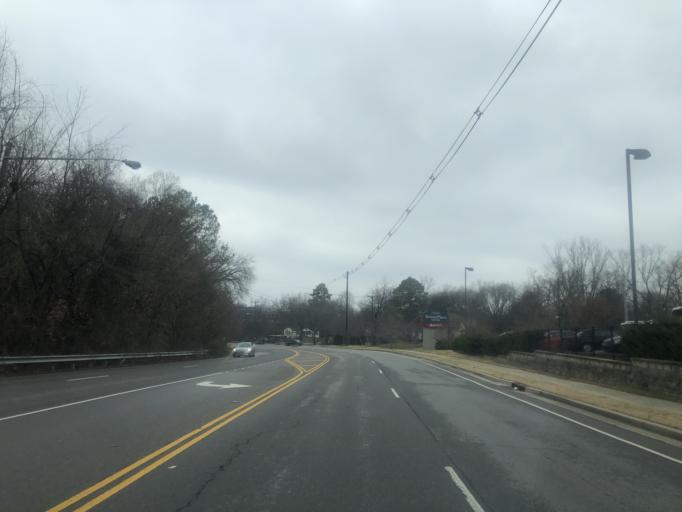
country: US
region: Tennessee
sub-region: Davidson County
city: Lakewood
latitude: 36.1499
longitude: -86.6693
